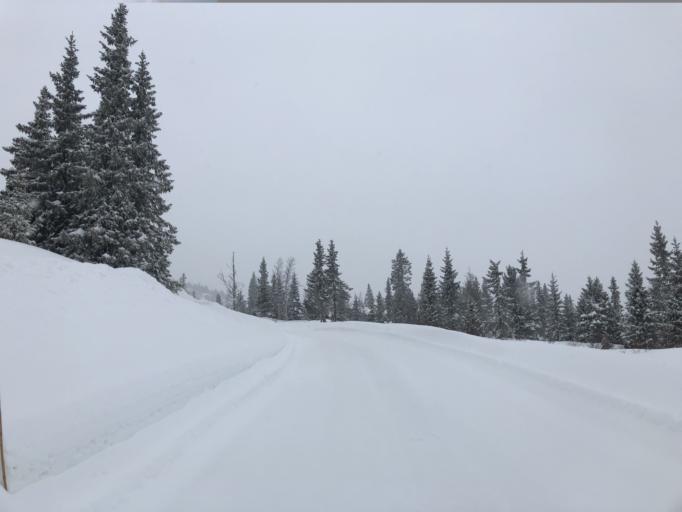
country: NO
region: Oppland
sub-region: Gausdal
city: Segalstad bru
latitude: 61.3280
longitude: 10.0555
